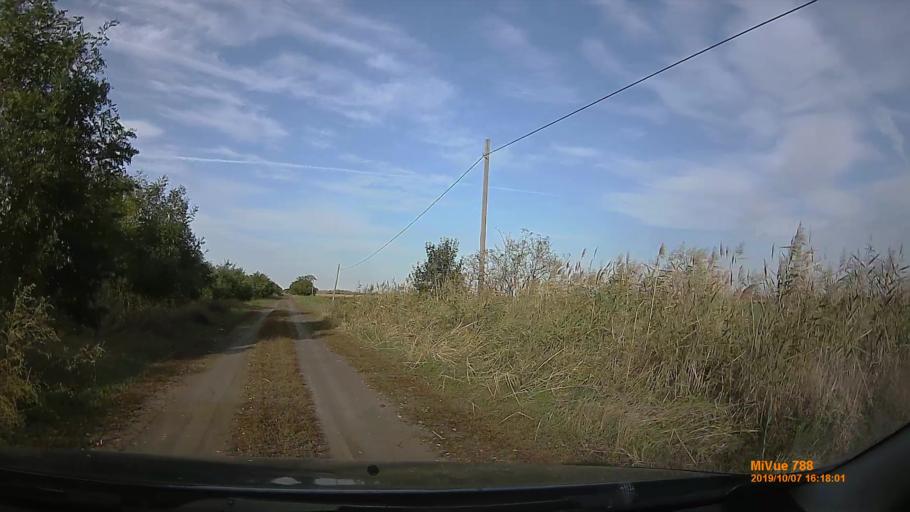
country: HU
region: Bekes
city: Szarvas
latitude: 46.8064
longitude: 20.6230
